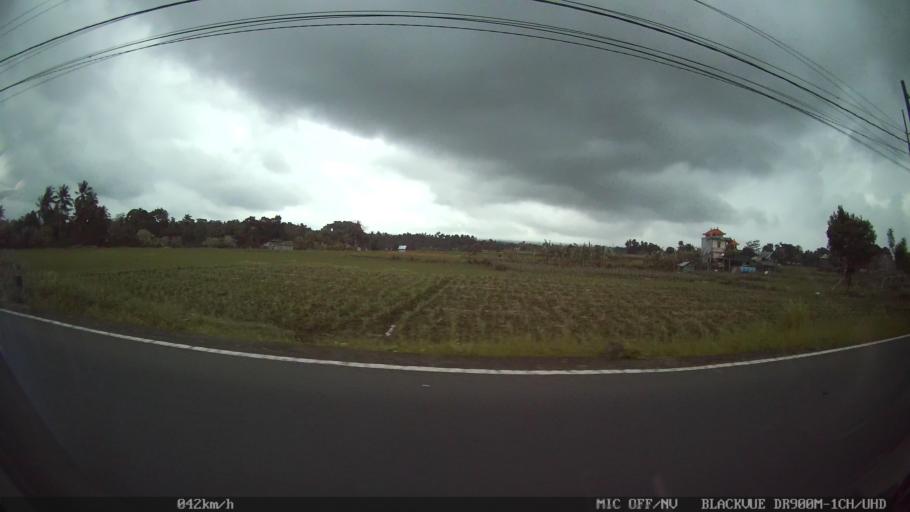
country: ID
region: Bali
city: Banjar Mambalkajanan
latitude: -8.5363
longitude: 115.2242
